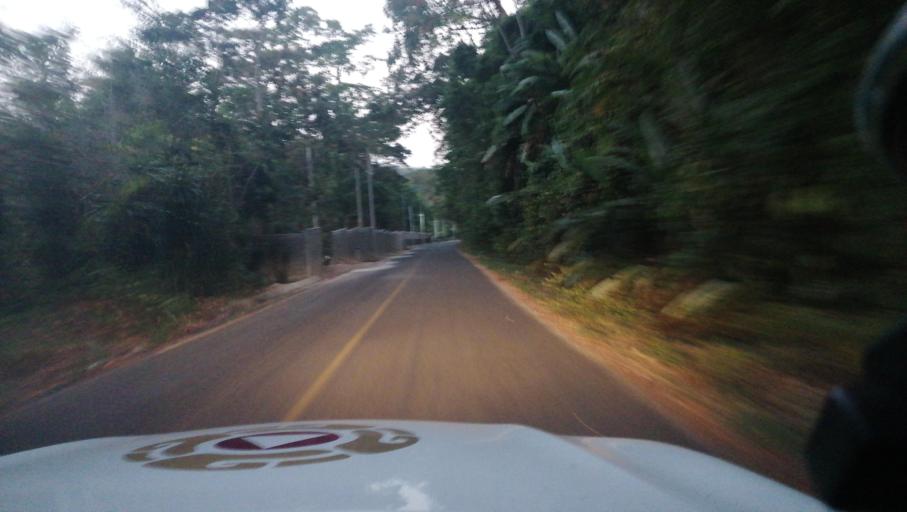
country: MX
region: Chiapas
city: Veinte de Noviembre
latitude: 14.9973
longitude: -92.2431
